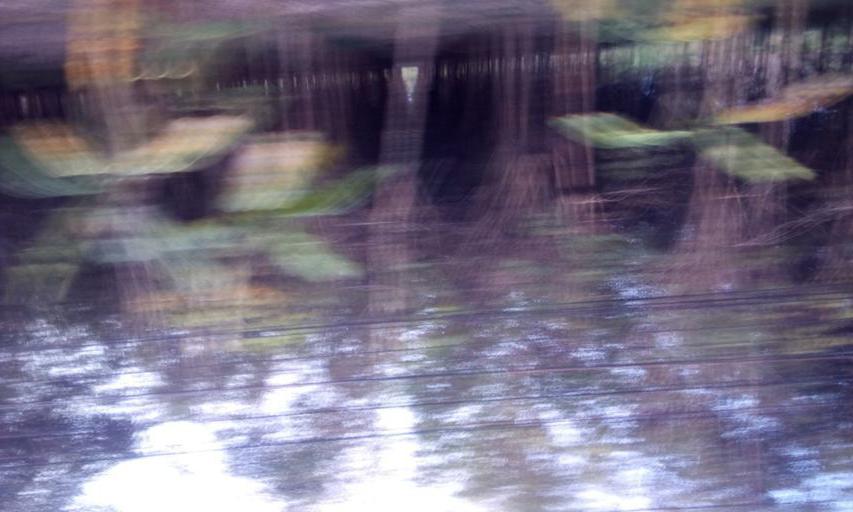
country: TH
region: Trat
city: Laem Ngop
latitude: 12.2629
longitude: 102.2957
